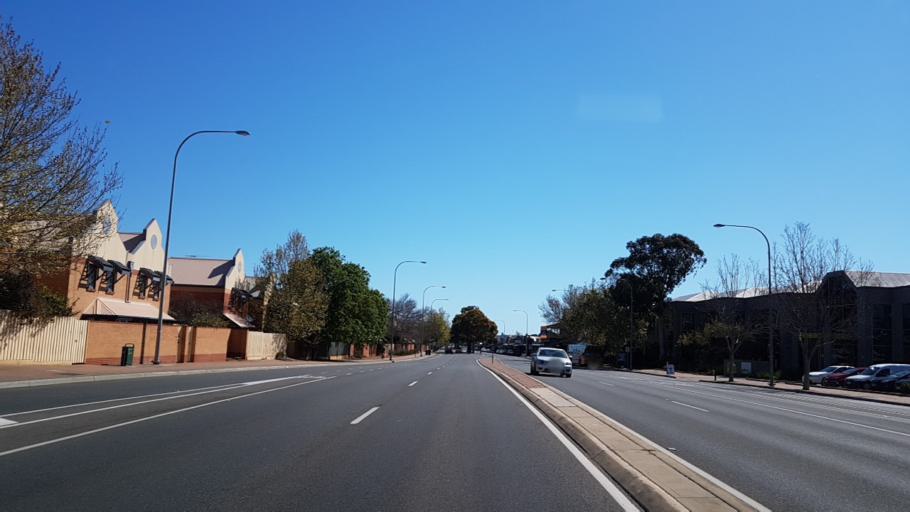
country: AU
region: South Australia
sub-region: City of West Torrens
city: Thebarton
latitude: -34.9234
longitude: 138.5775
